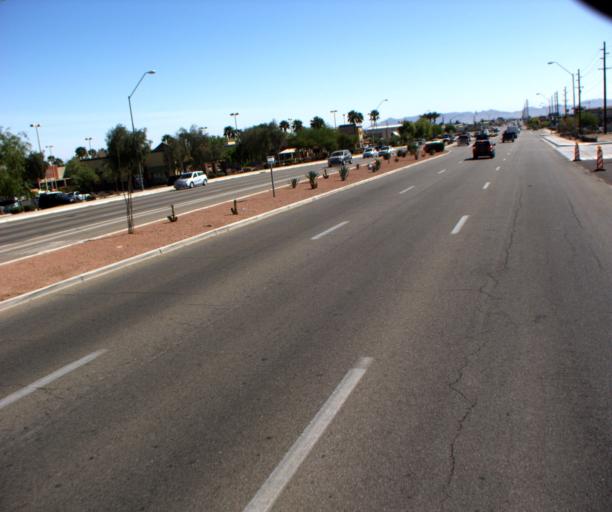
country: US
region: Arizona
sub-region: Yuma County
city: Yuma
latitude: 32.6985
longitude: -114.6026
